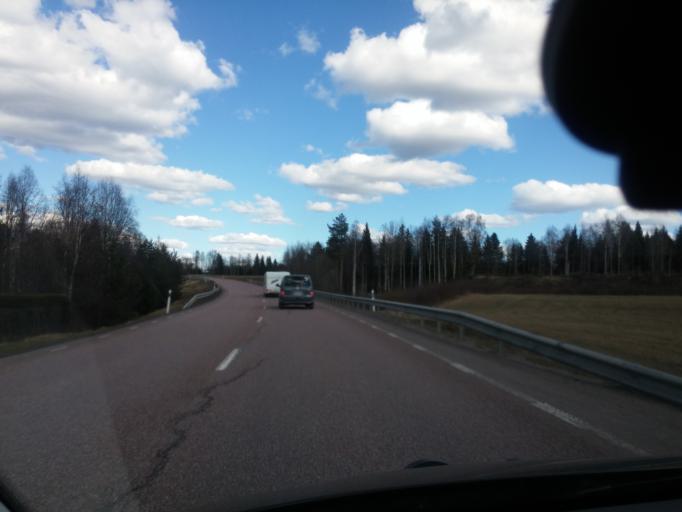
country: SE
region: Gaevleborg
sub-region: Ljusdals Kommun
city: Farila
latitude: 61.8090
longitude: 15.9506
